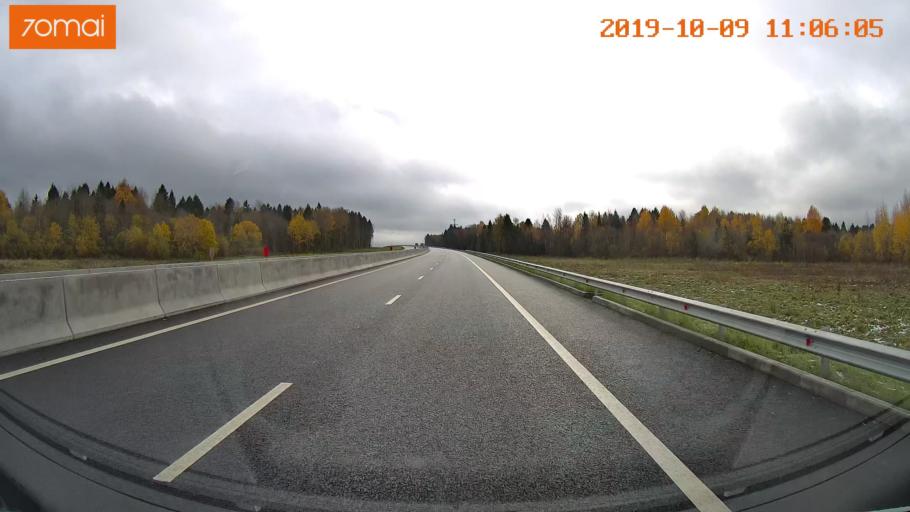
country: RU
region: Vologda
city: Molochnoye
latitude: 59.1913
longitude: 39.7584
